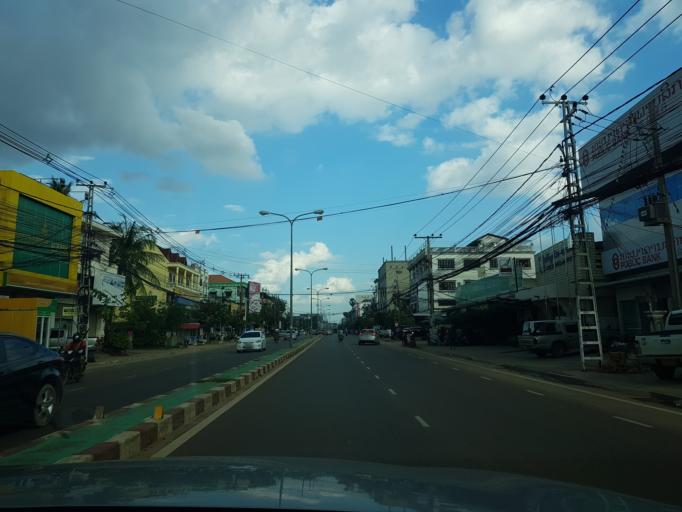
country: TH
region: Nong Khai
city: Si Chiang Mai
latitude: 17.9695
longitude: 102.5771
